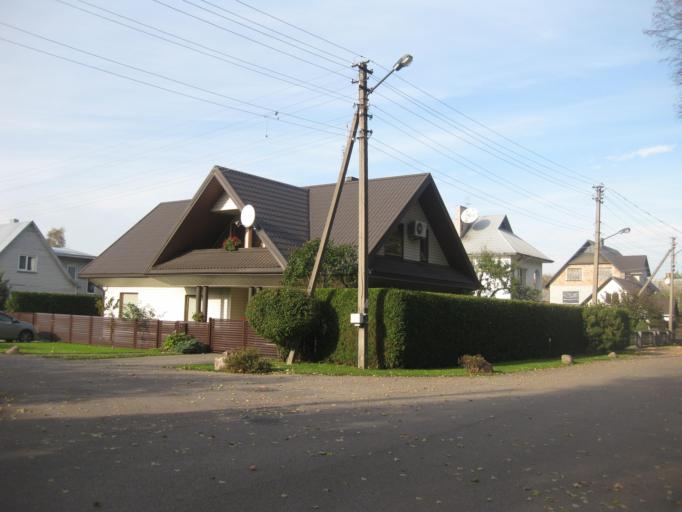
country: LT
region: Kauno apskritis
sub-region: Kaunas
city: Aleksotas
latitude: 54.8914
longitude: 23.8795
